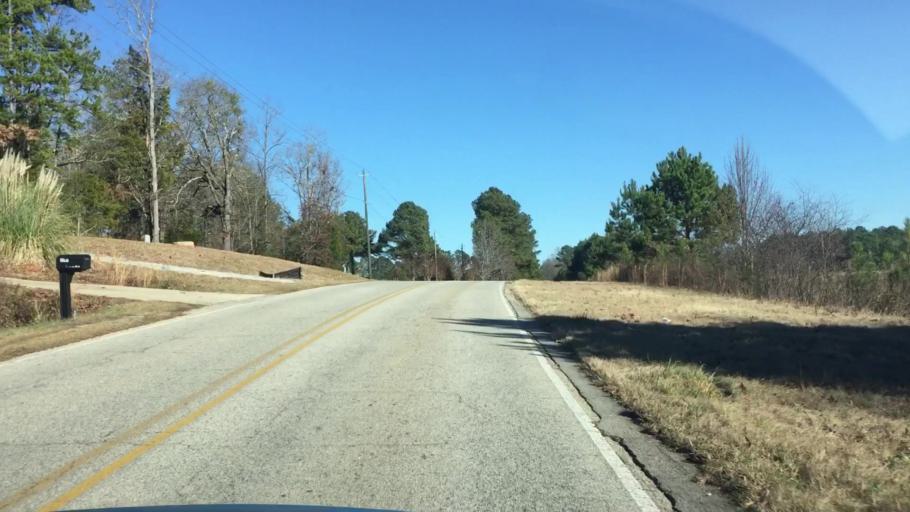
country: US
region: Georgia
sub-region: Henry County
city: McDonough
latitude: 33.4971
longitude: -84.0671
